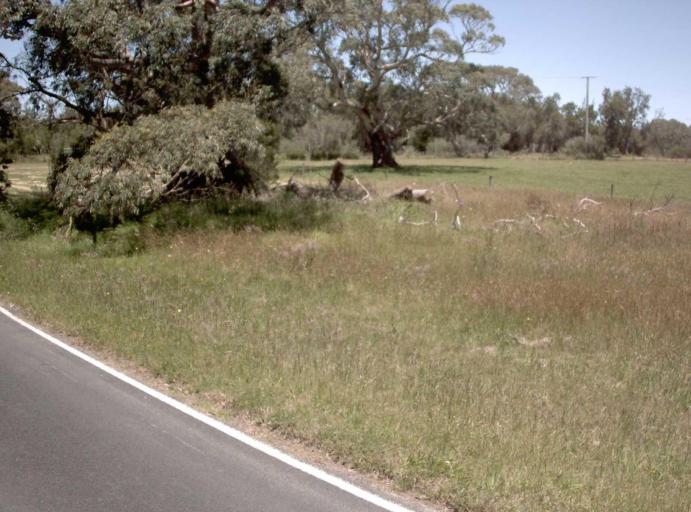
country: AU
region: Victoria
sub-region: Latrobe
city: Morwell
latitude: -38.8548
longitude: 146.2456
